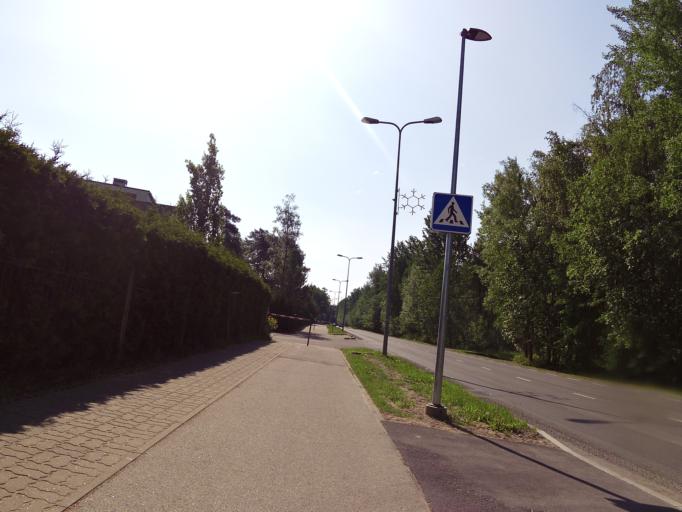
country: EE
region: Harju
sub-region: Harku vald
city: Tabasalu
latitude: 59.4416
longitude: 24.6200
